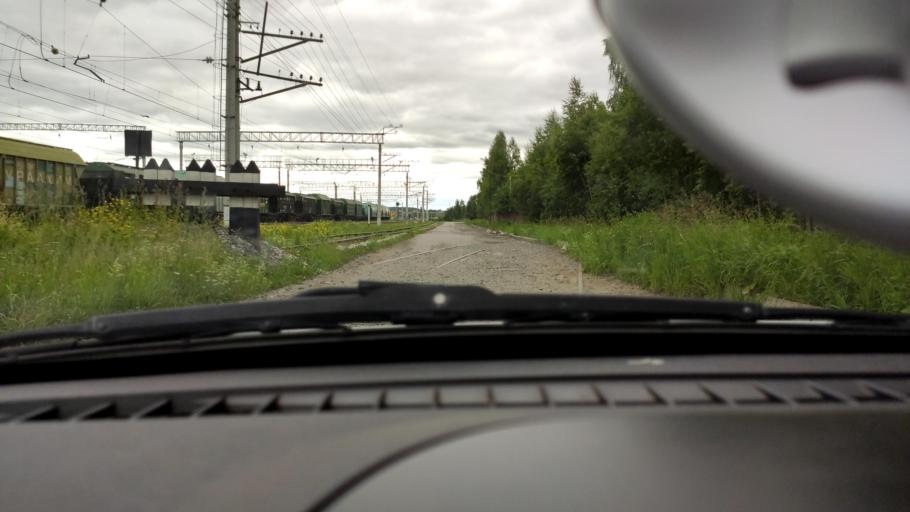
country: RU
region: Perm
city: Ferma
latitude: 57.8913
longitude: 56.2990
